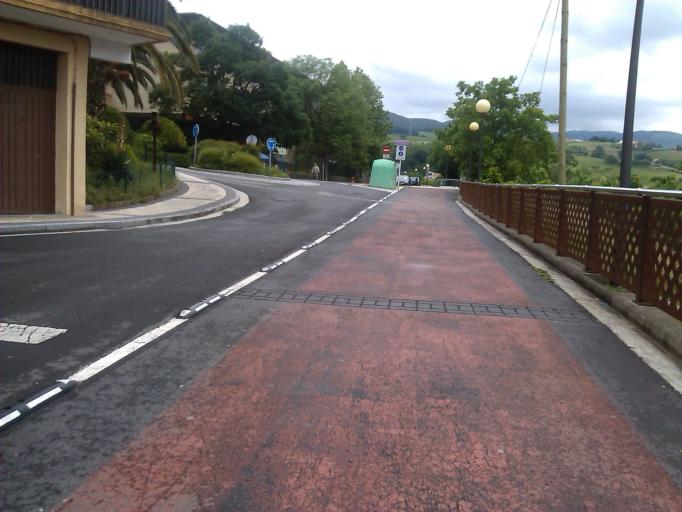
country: ES
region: Basque Country
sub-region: Provincia de Guipuzcoa
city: Andoain
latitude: 43.2171
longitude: -2.0195
